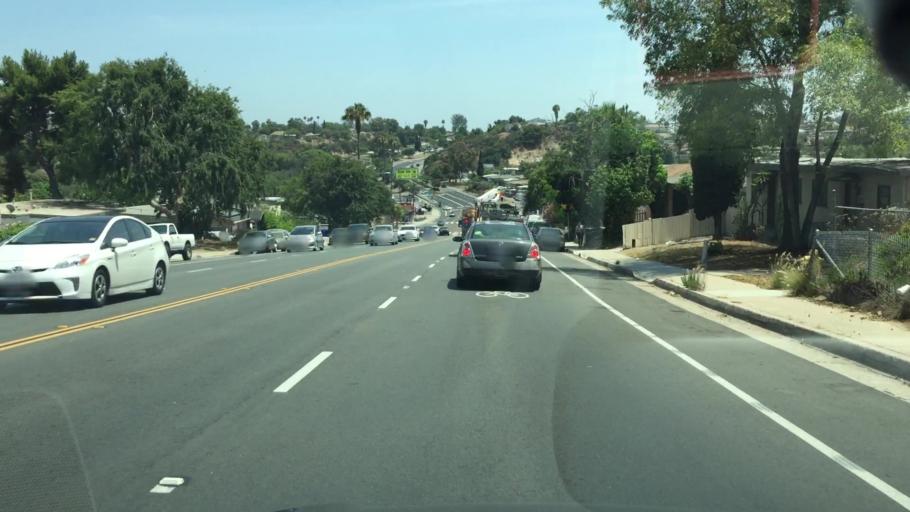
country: US
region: California
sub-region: San Diego County
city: Lemon Grove
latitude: 32.7549
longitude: -117.0655
